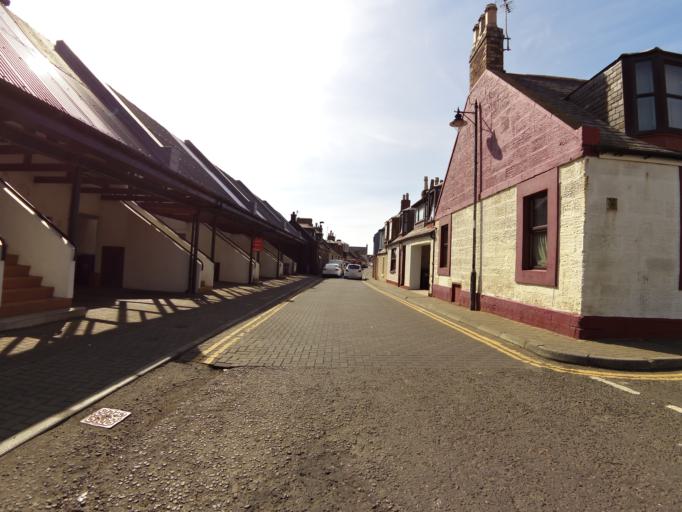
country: GB
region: Scotland
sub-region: Angus
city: Arbroath
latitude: 56.5570
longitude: -2.5777
